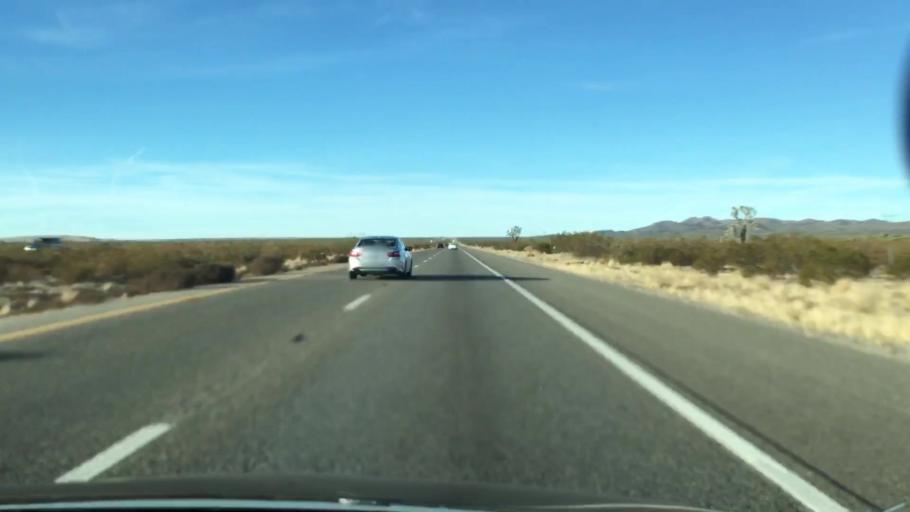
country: US
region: Nevada
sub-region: Clark County
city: Sandy Valley
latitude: 35.4255
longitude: -115.7274
